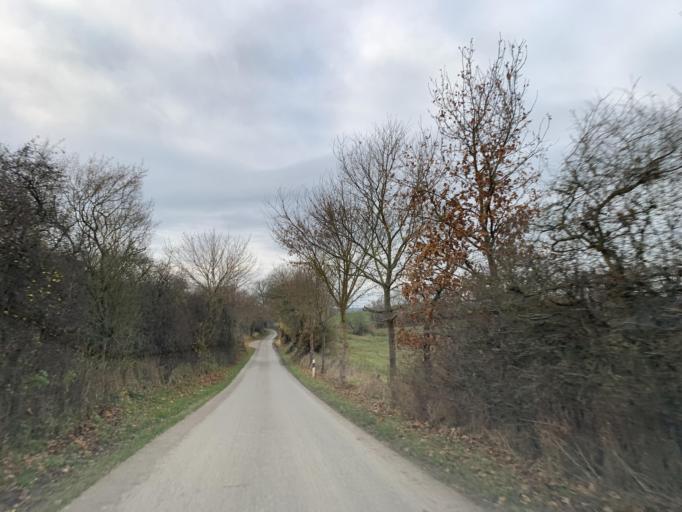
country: DE
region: Mecklenburg-Vorpommern
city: Carpin
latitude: 53.3988
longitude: 13.2202
